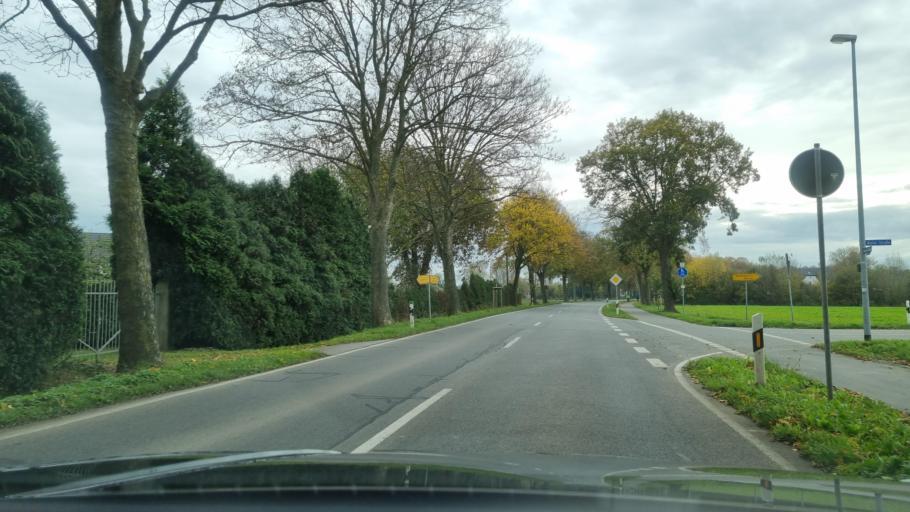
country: NL
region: Gelderland
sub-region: Gemeente Zevenaar
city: Zevenaar
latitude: 51.8490
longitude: 6.0792
